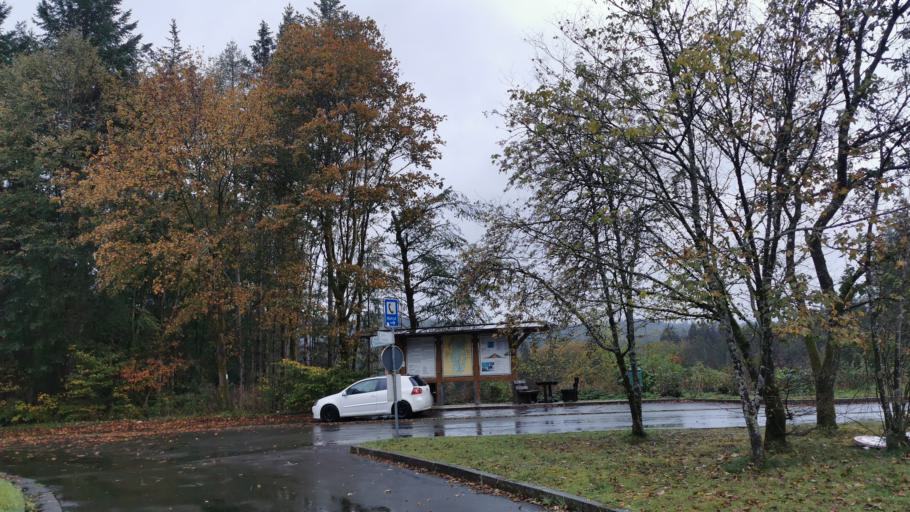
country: DE
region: Bavaria
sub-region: Upper Franconia
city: Steinwiesen
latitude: 50.3240
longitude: 11.4876
